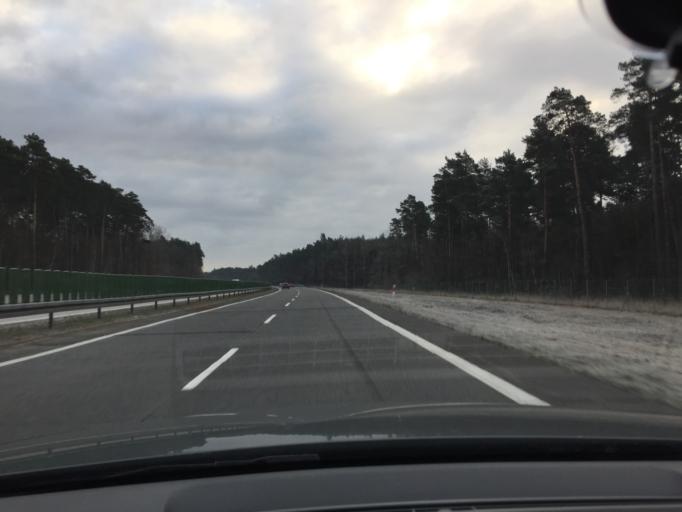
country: PL
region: Lubusz
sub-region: Powiat zarski
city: Lipinki Luzyckie
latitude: 51.6152
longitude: 14.9233
